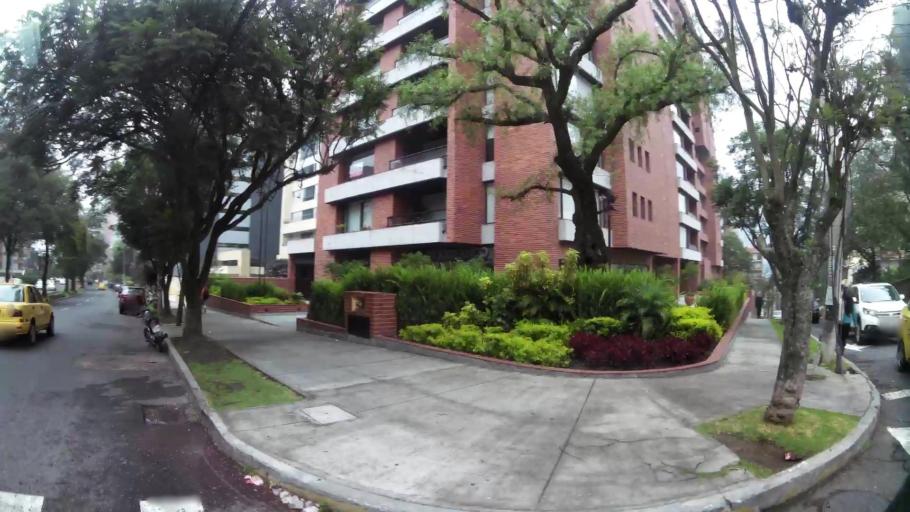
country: EC
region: Pichincha
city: Quito
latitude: -0.1948
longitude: -78.4779
